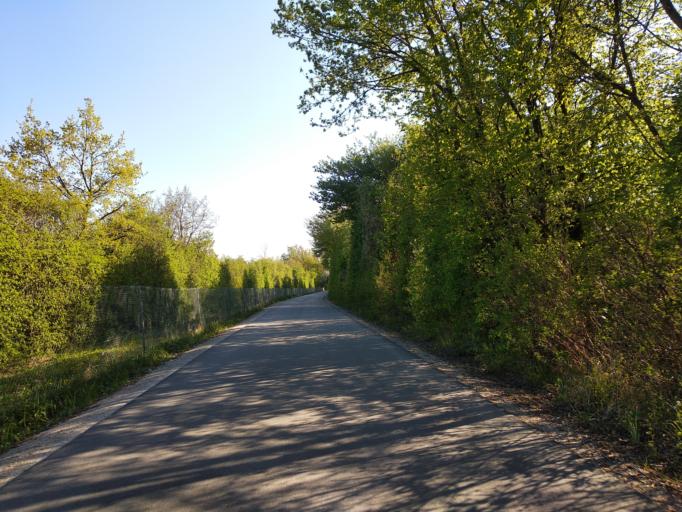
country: DE
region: Bavaria
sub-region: Upper Bavaria
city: Grasbrunn
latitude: 48.0733
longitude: 11.7361
